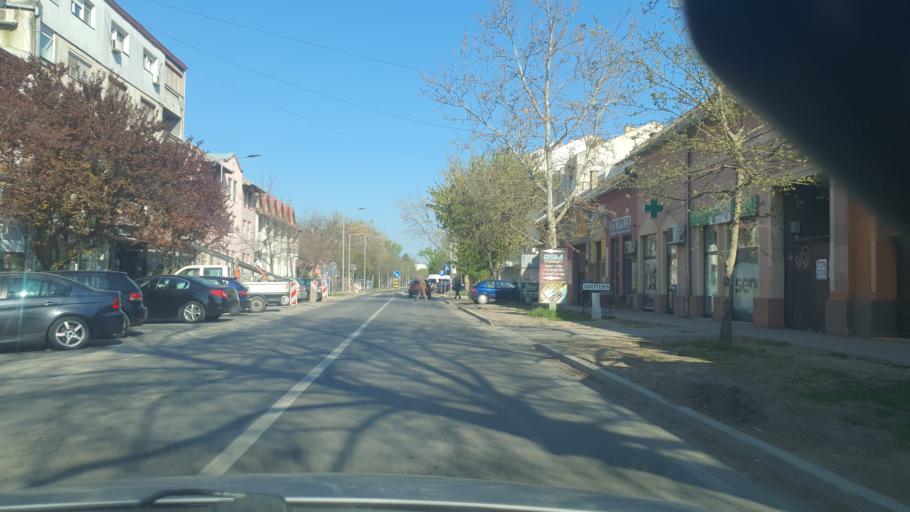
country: RS
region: Autonomna Pokrajina Vojvodina
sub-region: Zapadnobacki Okrug
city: Kula
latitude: 45.6100
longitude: 19.5319
